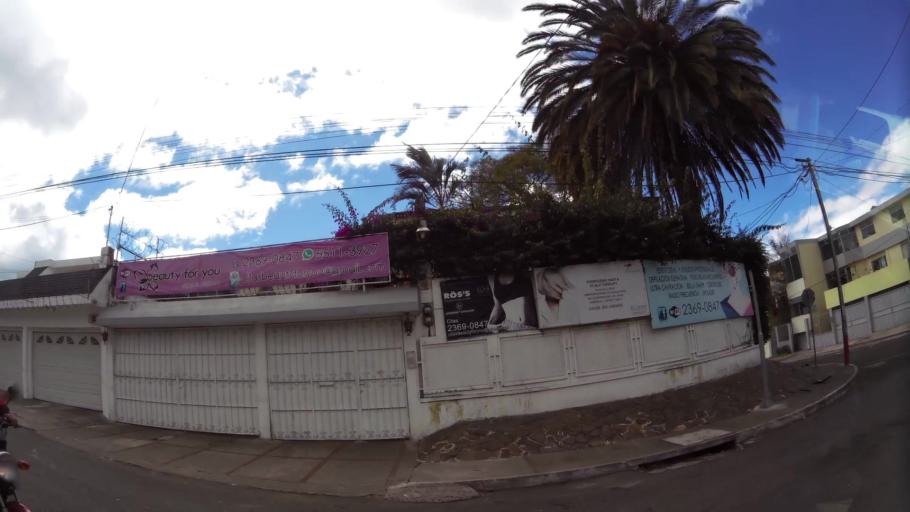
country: GT
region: Guatemala
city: Santa Catarina Pinula
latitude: 14.5967
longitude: -90.4975
